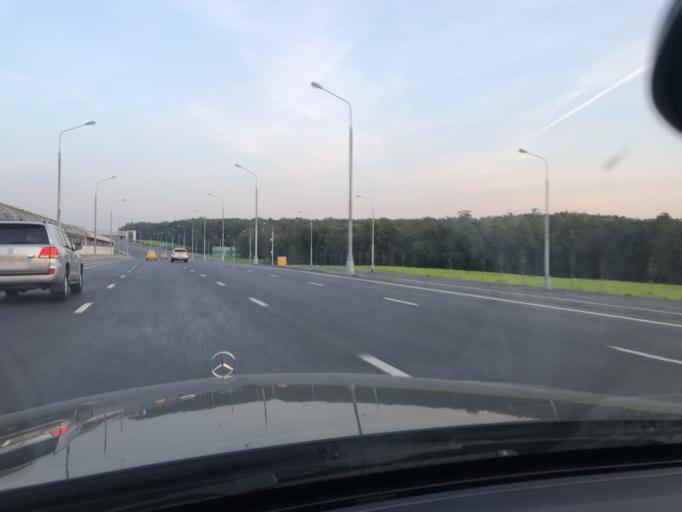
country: RU
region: Moskovskaya
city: Mosrentgen
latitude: 55.5901
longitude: 37.4242
